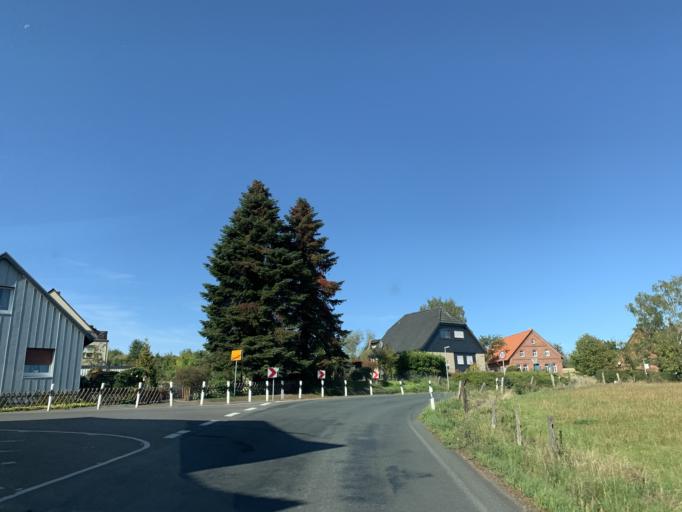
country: DE
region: North Rhine-Westphalia
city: Porta Westfalica
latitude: 52.1993
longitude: 8.9695
